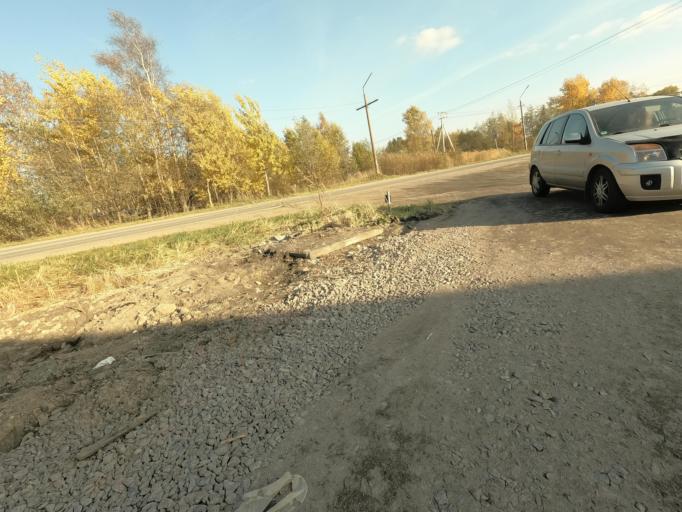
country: RU
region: Leningrad
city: Mga
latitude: 59.7481
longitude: 31.0626
